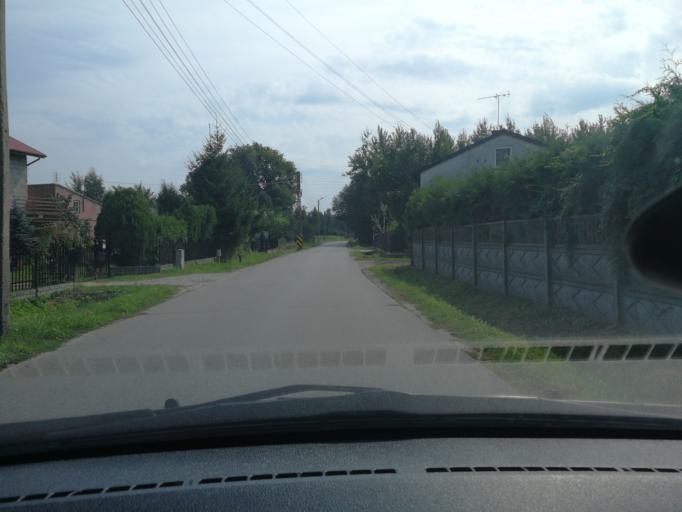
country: PL
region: Lodz Voivodeship
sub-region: Skierniewice
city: Skierniewice
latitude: 51.9744
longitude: 20.1089
